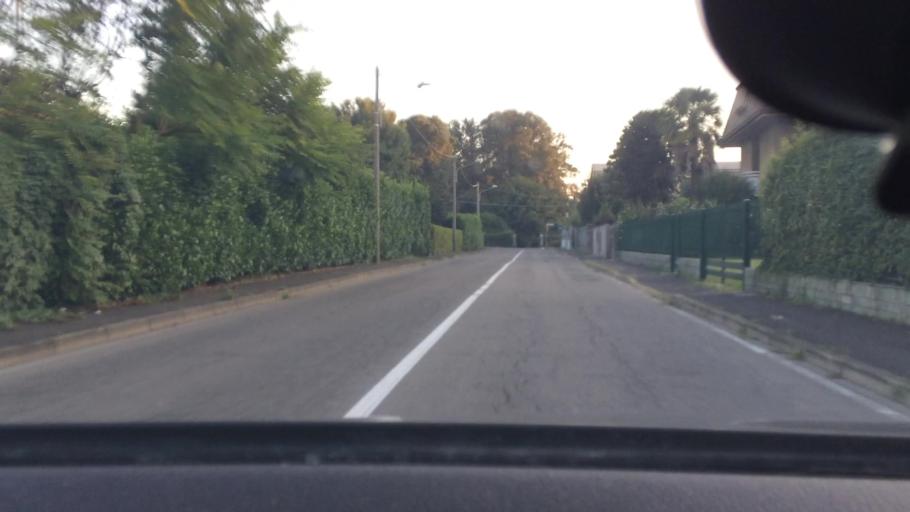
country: IT
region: Lombardy
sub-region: Provincia di Como
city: Rovello Porro
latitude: 45.6515
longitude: 9.0444
